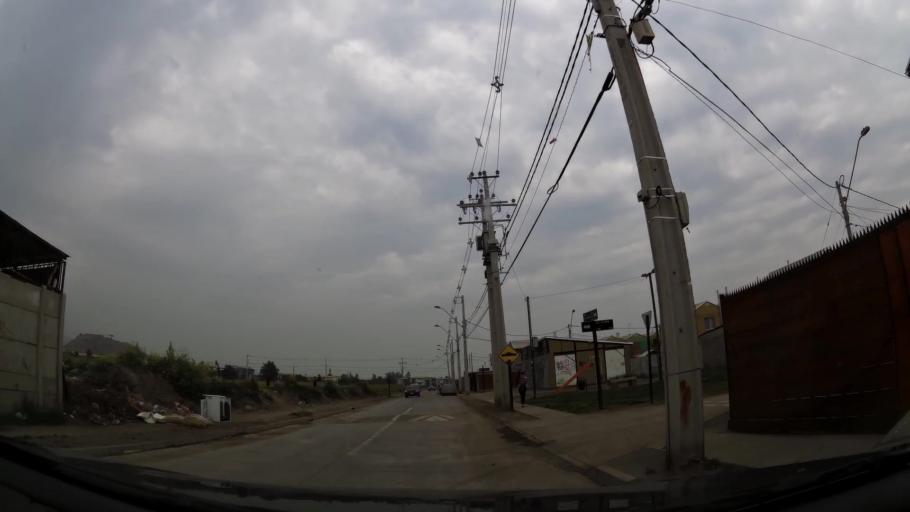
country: CL
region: Santiago Metropolitan
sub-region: Provincia de Chacabuco
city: Chicureo Abajo
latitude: -33.1857
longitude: -70.6661
